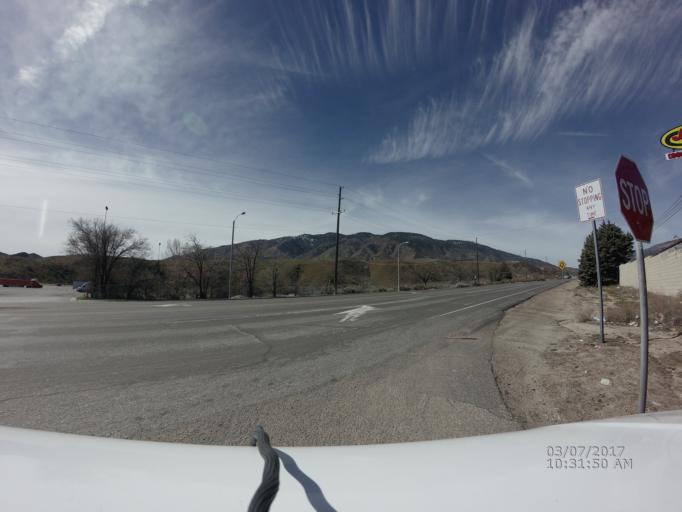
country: US
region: California
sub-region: Kern County
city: Lebec
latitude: 34.8179
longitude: -118.8895
